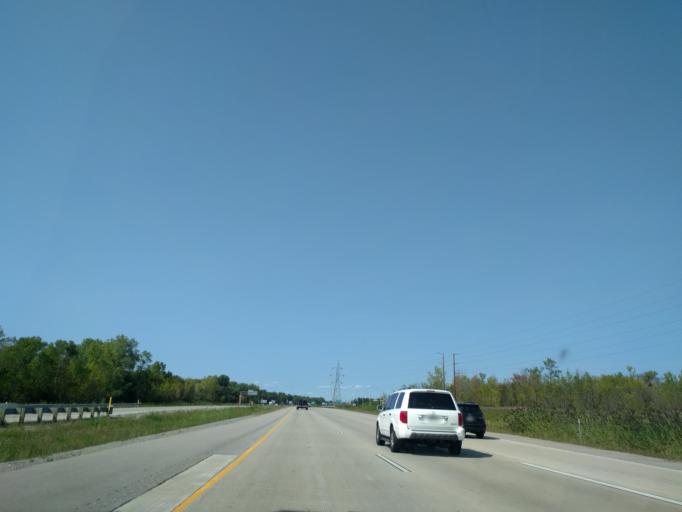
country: US
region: Wisconsin
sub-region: Brown County
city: Suamico
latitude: 44.5951
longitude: -88.0491
